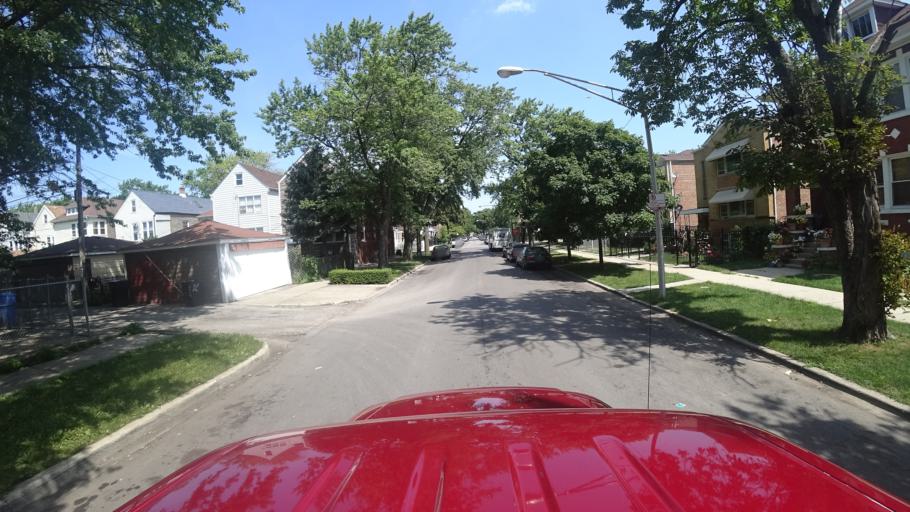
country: US
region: Illinois
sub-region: Cook County
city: Hometown
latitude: 41.7967
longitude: -87.6988
